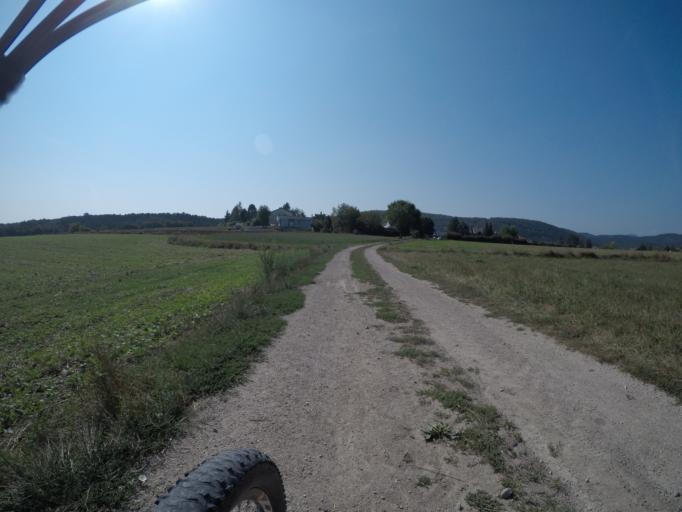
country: AT
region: Lower Austria
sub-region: Politischer Bezirk Baden
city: Hirtenberg
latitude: 47.9397
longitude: 16.1639
